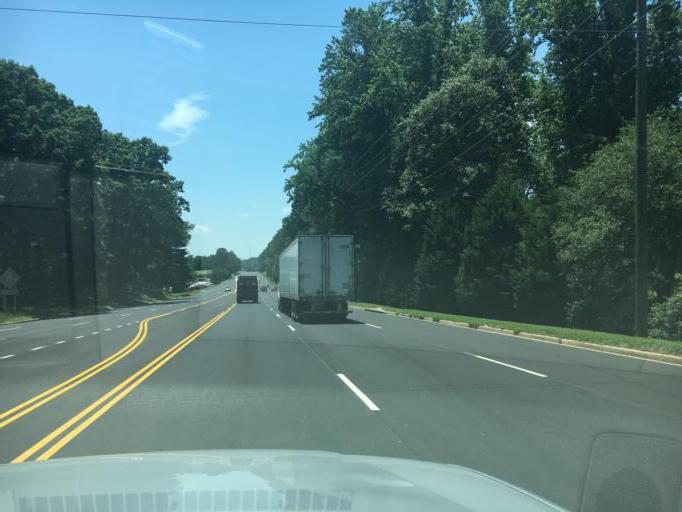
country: US
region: South Carolina
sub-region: Greenville County
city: Travelers Rest
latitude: 34.9356
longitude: -82.4476
